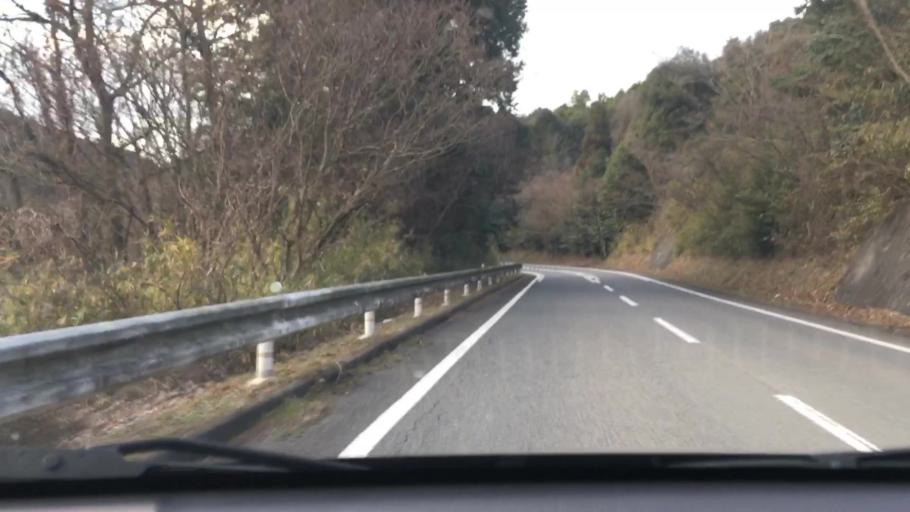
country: JP
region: Oita
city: Hiji
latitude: 33.4127
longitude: 131.4239
